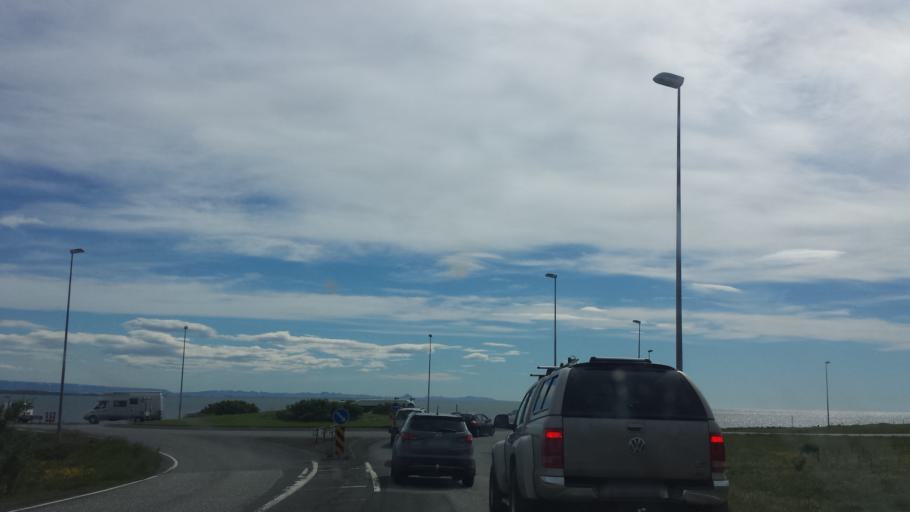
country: IS
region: West
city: Akranes
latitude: 64.3089
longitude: -21.9119
